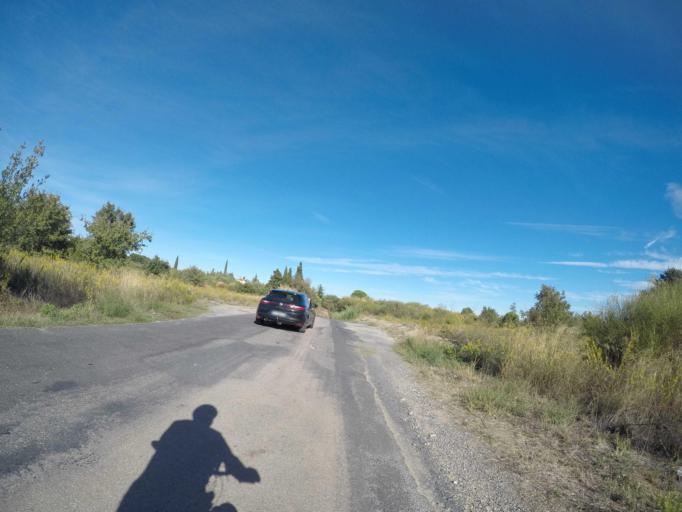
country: FR
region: Languedoc-Roussillon
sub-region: Departement des Pyrenees-Orientales
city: Trouillas
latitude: 42.6063
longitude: 2.8054
